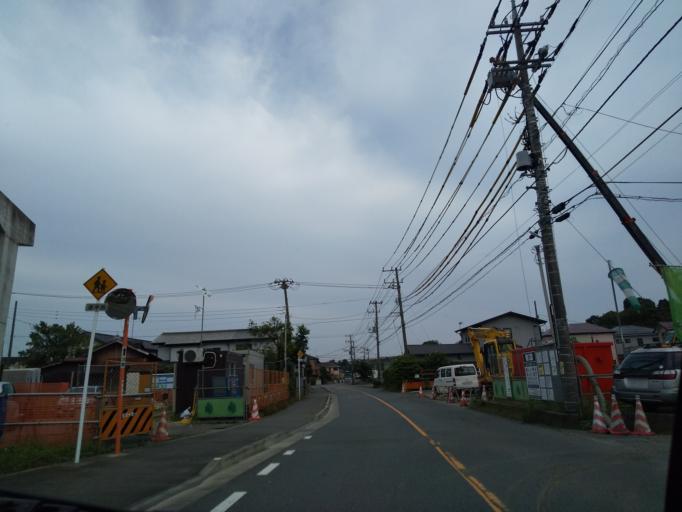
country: JP
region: Kanagawa
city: Zama
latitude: 35.4822
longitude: 139.3514
